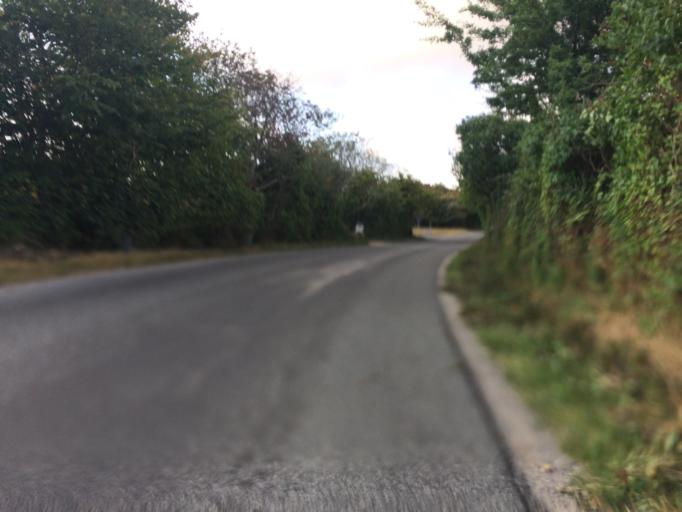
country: DK
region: Central Jutland
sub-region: Holstebro Kommune
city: Vinderup
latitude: 56.6148
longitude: 8.7625
